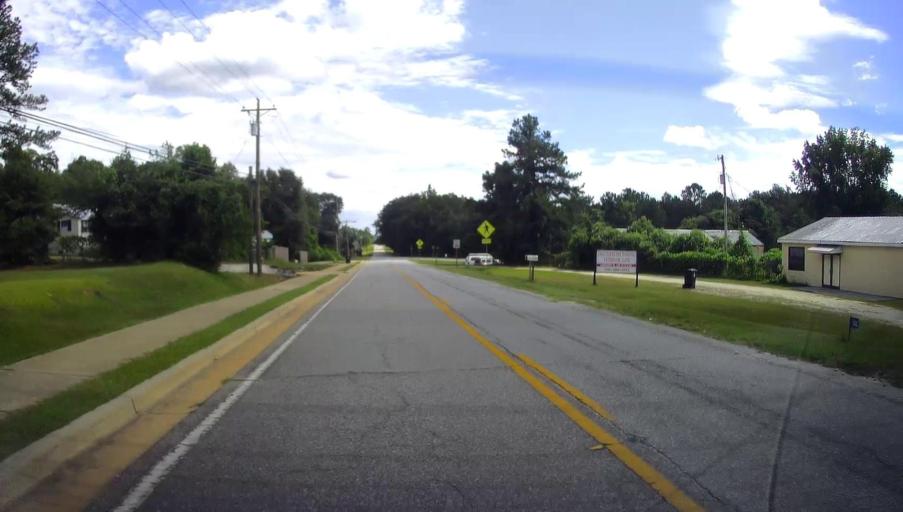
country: US
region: Georgia
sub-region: Chattahoochee County
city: Cusseta
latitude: 32.2996
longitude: -84.7705
